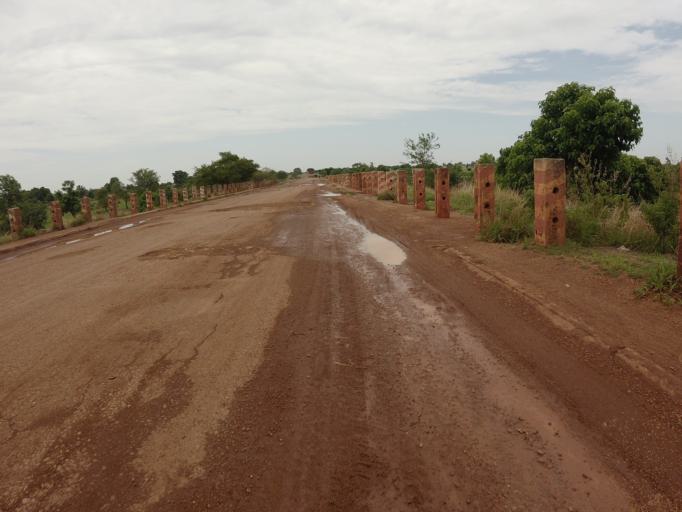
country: GH
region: Upper East
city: Bawku
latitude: 11.0025
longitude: -0.3824
